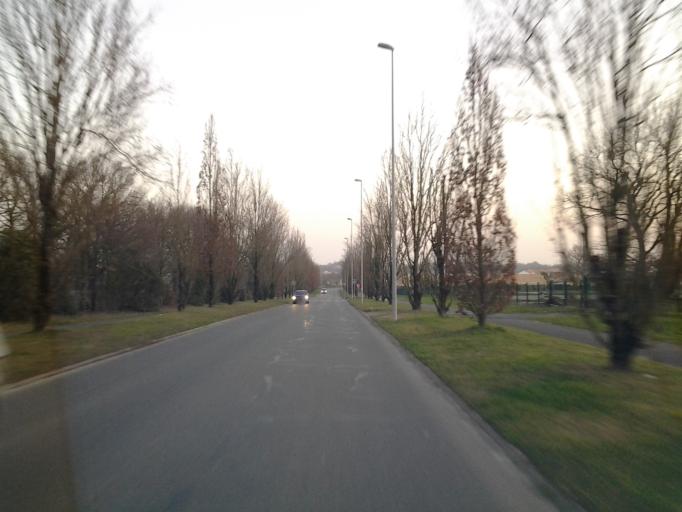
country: FR
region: Pays de la Loire
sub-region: Departement de la Vendee
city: La Roche-sur-Yon
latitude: 46.6575
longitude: -1.4115
